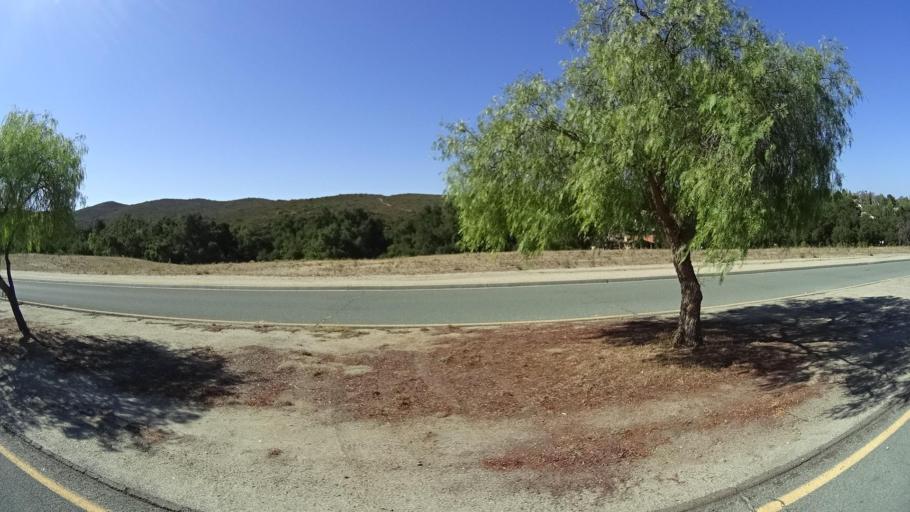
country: US
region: California
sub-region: San Diego County
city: San Diego Country Estates
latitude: 33.0025
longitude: -116.7725
